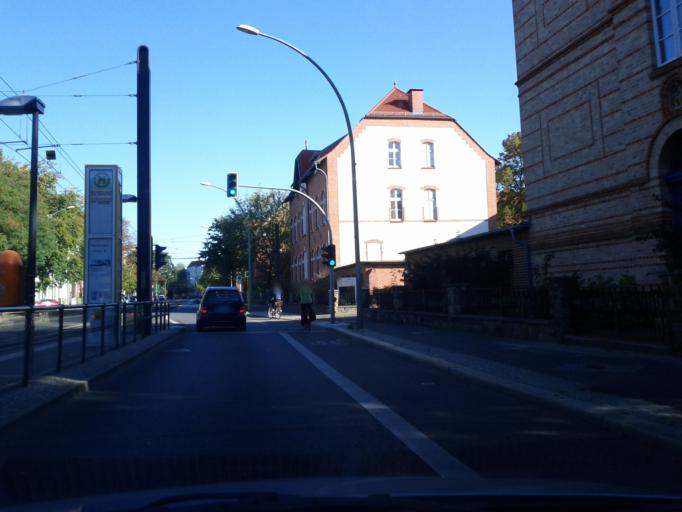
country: DE
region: Berlin
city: Pankow
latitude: 52.5714
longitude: 13.3985
